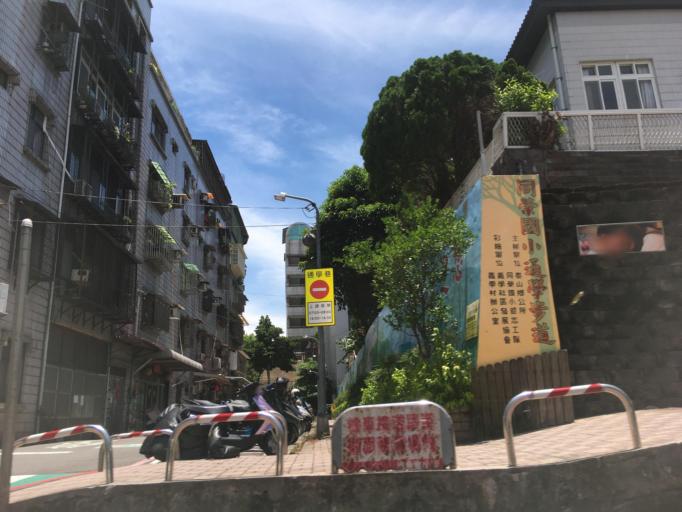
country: TW
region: Taipei
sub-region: Taipei
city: Banqiao
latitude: 25.0545
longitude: 121.4287
